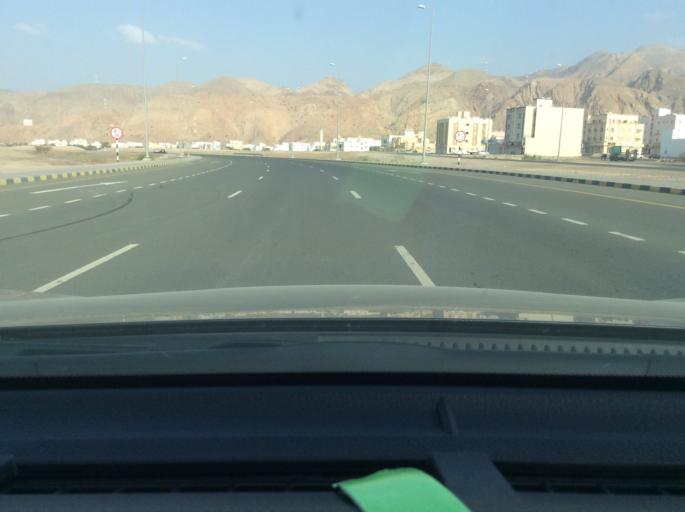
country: OM
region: Muhafazat Masqat
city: Bawshar
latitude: 23.5019
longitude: 58.5014
